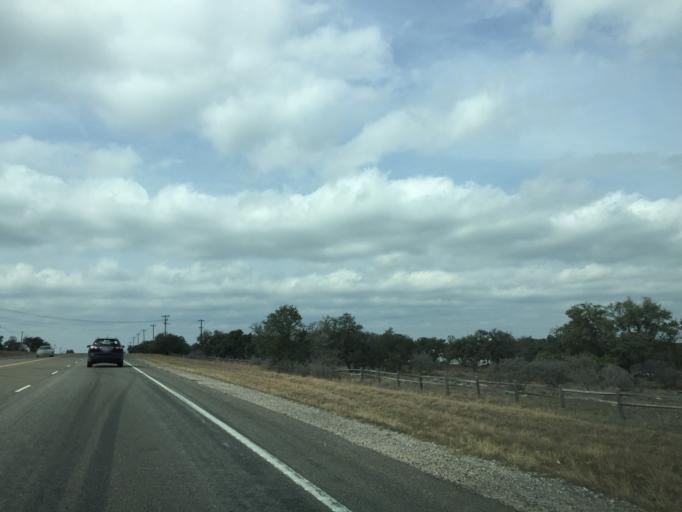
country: US
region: Texas
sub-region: Burnet County
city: Marble Falls
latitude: 30.4885
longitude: -98.2165
